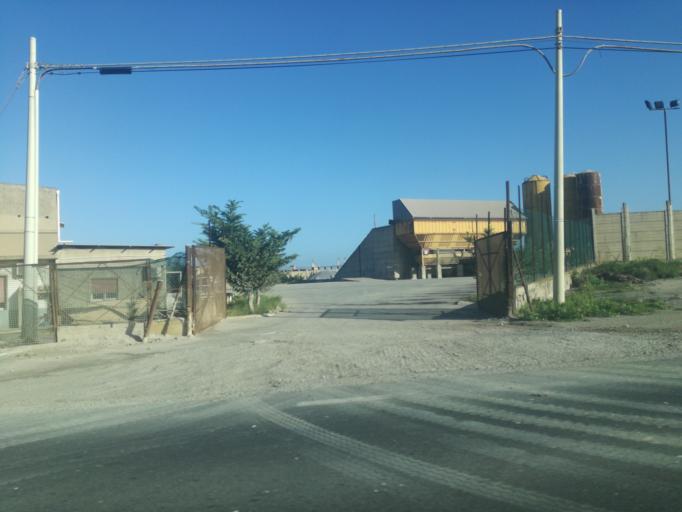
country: IT
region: Sicily
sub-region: Provincia di Caltanissetta
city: Gela
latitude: 37.0611
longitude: 14.2756
